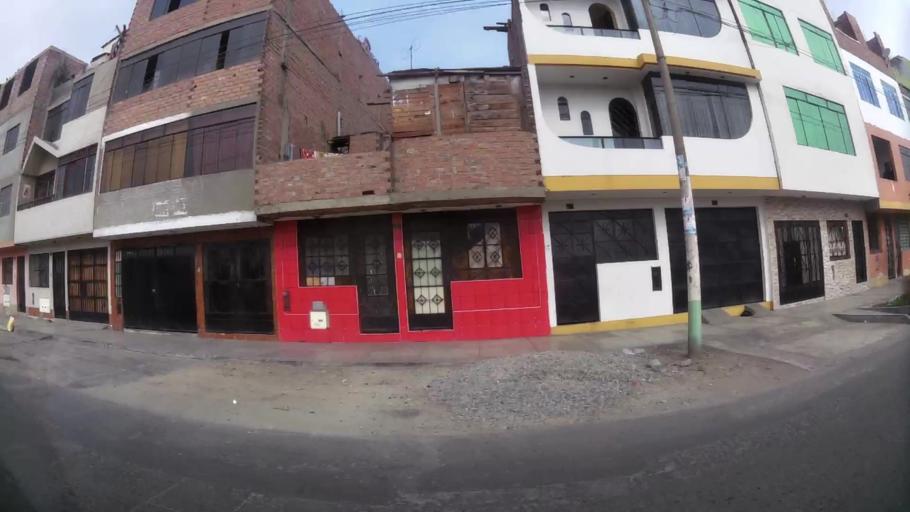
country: PE
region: Callao
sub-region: Callao
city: Callao
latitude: -12.0242
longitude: -77.0935
